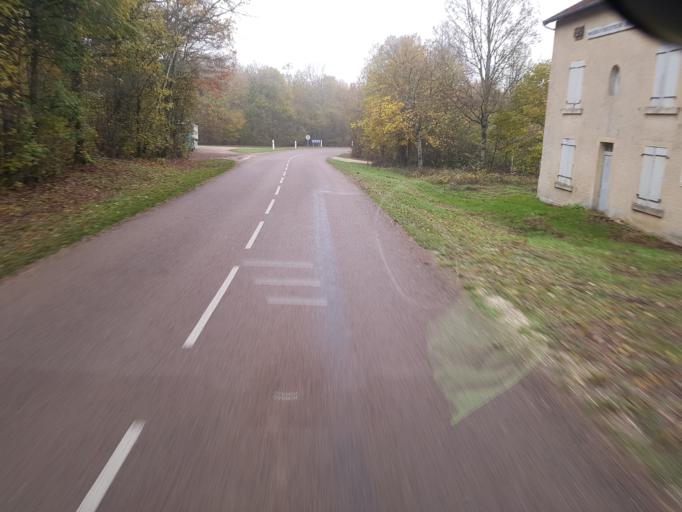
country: FR
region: Bourgogne
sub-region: Departement de la Cote-d'Or
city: Messigny-et-Vantoux
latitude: 47.5709
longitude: 4.8992
